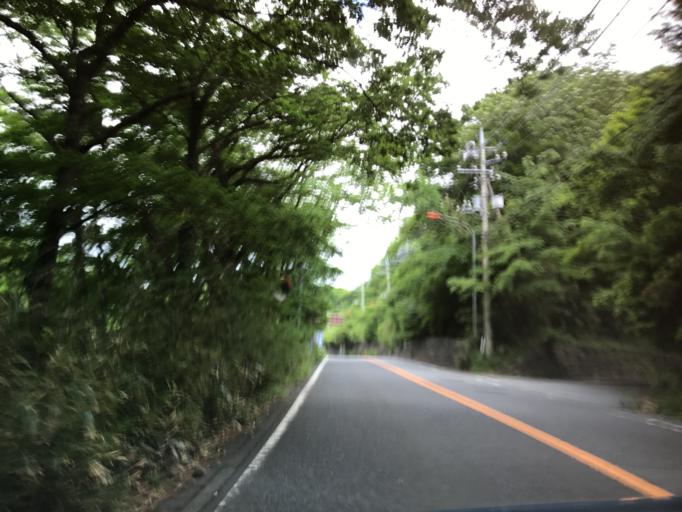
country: JP
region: Kanagawa
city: Hakone
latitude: 35.2644
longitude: 139.0232
